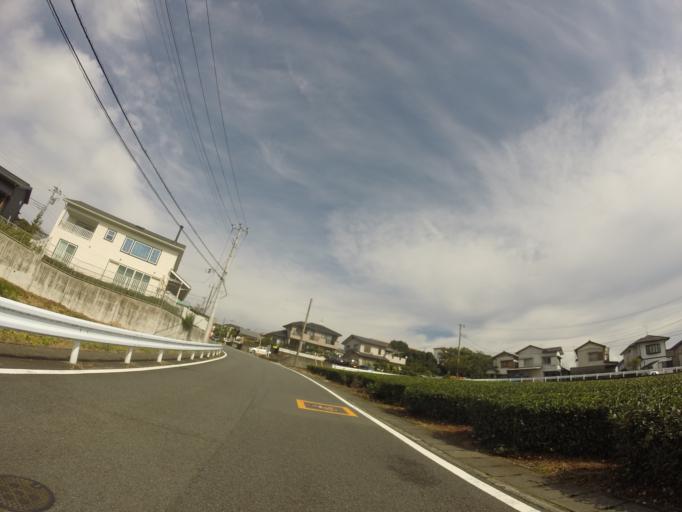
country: JP
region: Shizuoka
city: Fuji
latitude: 35.1909
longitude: 138.6934
